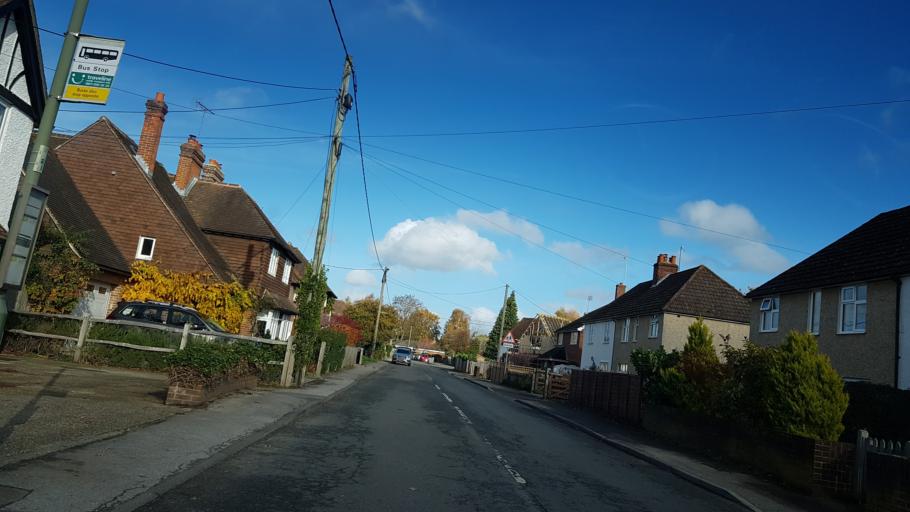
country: GB
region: England
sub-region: Surrey
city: Elstead
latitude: 51.1792
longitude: -0.7097
